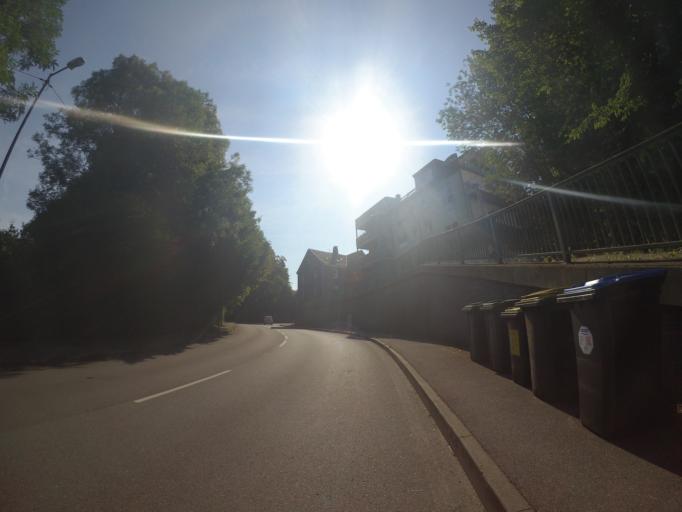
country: DE
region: North Rhine-Westphalia
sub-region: Regierungsbezirk Arnsberg
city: Schwelm
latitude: 51.2491
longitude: 7.2892
